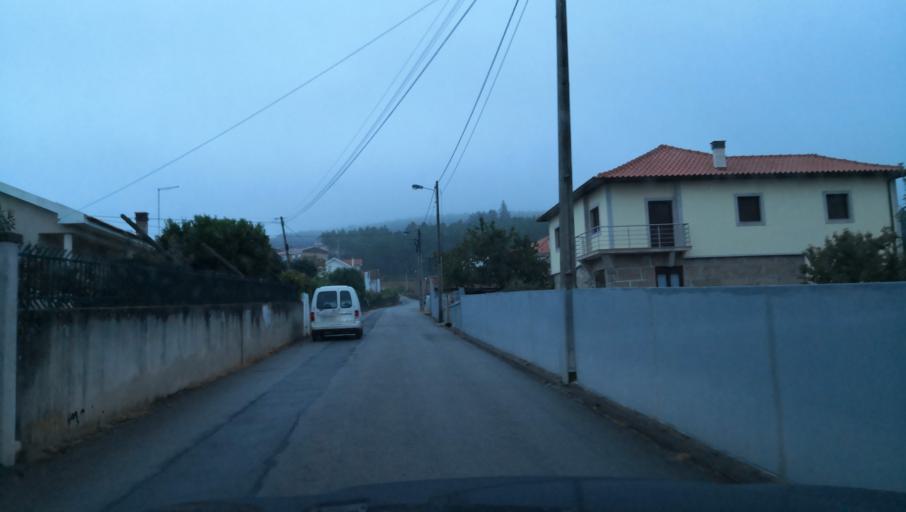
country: PT
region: Vila Real
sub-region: Sabrosa
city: Sabrosa
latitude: 41.2679
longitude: -7.6195
